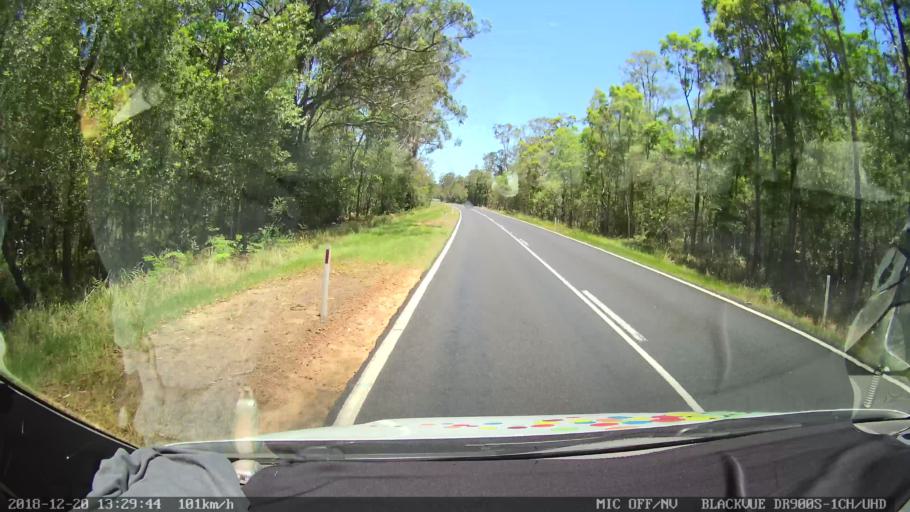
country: AU
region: New South Wales
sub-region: Clarence Valley
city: Gordon
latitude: -29.1935
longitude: 152.9908
